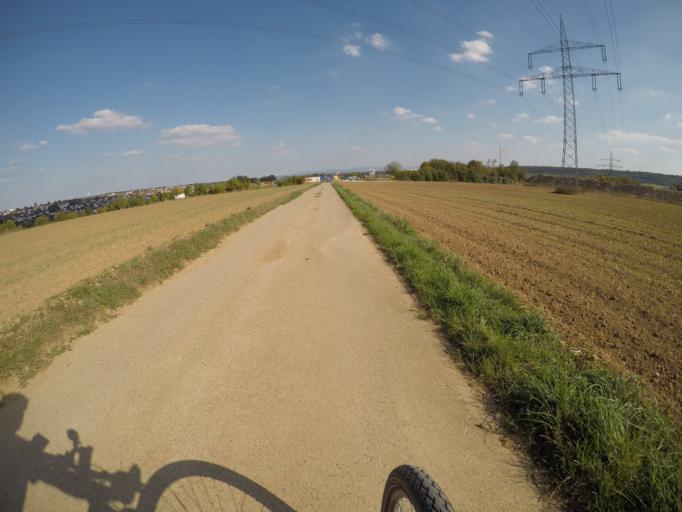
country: DE
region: Baden-Wuerttemberg
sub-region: Regierungsbezirk Stuttgart
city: Denkendorf
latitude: 48.6947
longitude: 9.2982
